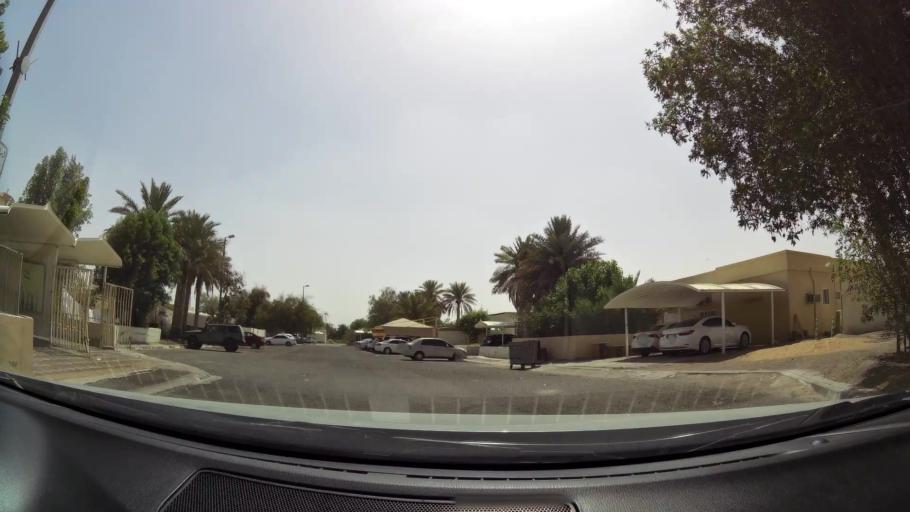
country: AE
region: Abu Dhabi
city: Al Ain
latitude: 24.2301
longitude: 55.7010
